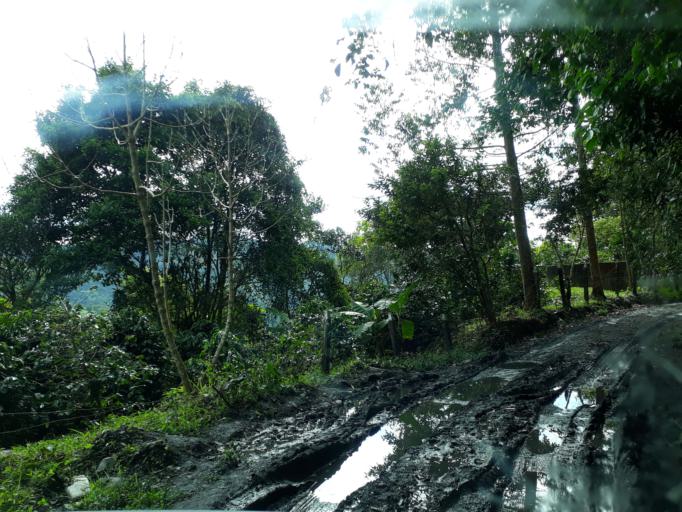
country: CO
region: Cundinamarca
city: Pacho
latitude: 5.1684
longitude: -74.2415
